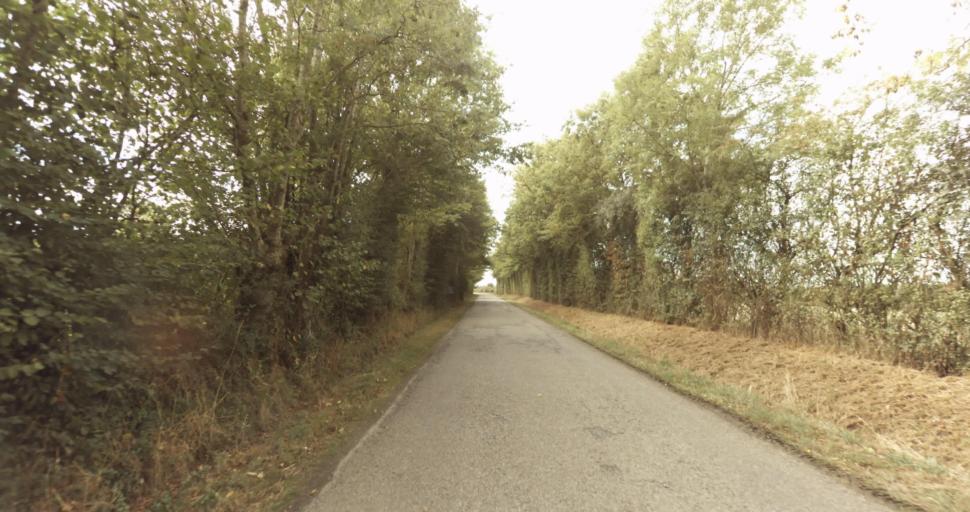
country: FR
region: Lower Normandy
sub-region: Departement du Calvados
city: La Vespiere
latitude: 48.9707
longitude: 0.3758
